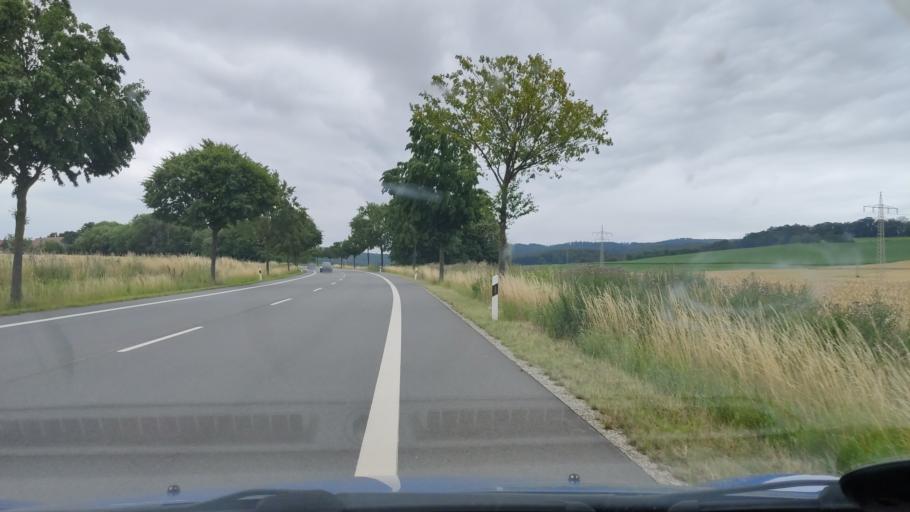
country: DE
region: Lower Saxony
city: Dielmissen
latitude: 51.9647
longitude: 9.6003
